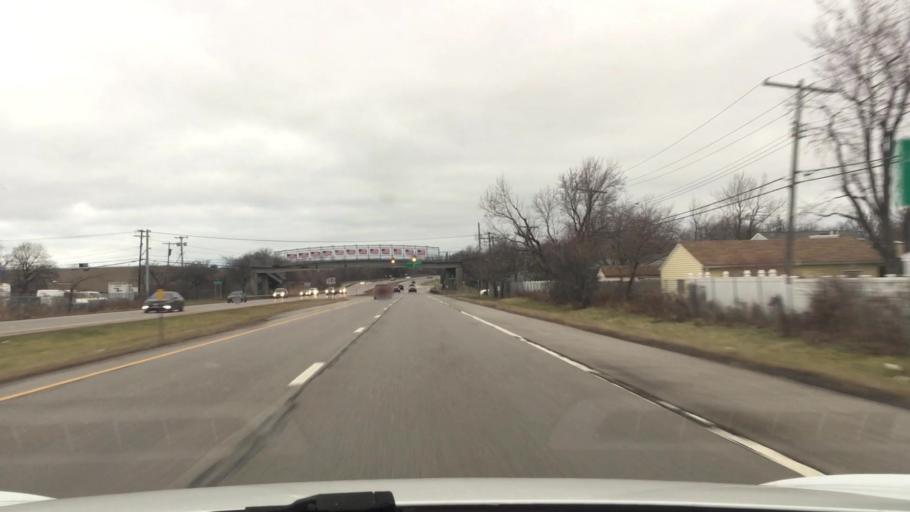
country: US
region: New York
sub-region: Erie County
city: Tonawanda
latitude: 43.0067
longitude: -78.8590
